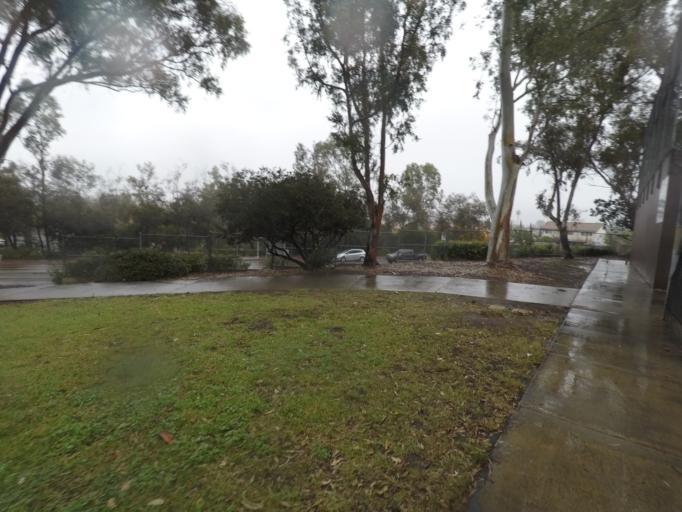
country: US
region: California
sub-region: San Diego County
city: San Diego
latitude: 32.7933
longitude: -117.1702
